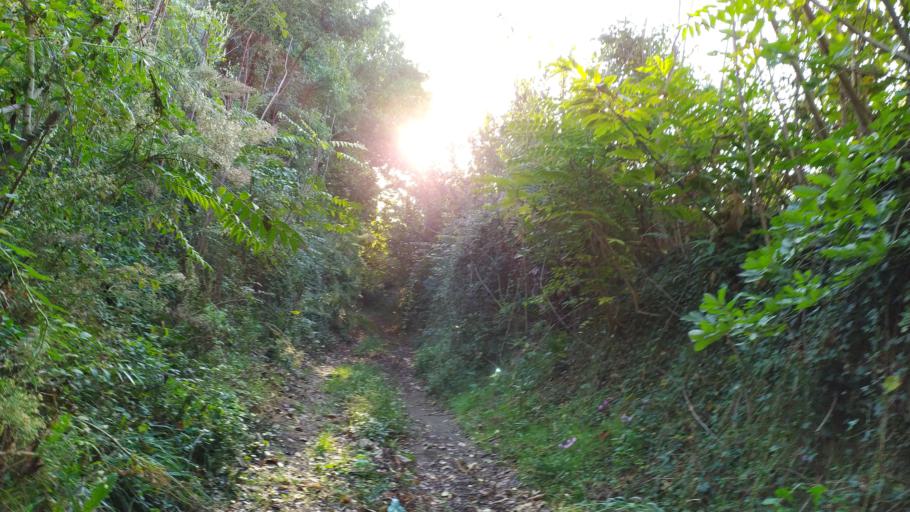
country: IT
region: Campania
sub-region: Provincia di Salerno
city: Lanzara
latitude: 40.7762
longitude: 14.6633
